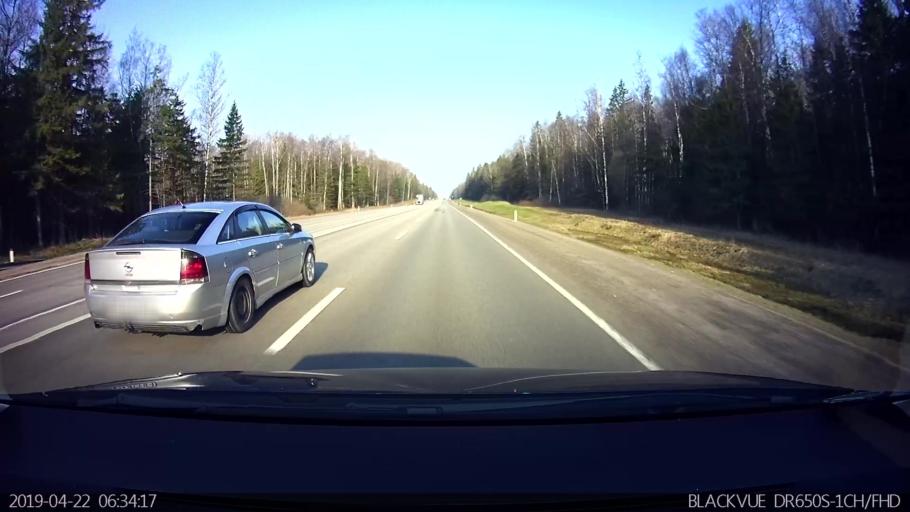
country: RU
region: Moskovskaya
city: Uvarovka
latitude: 55.4727
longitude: 35.5040
